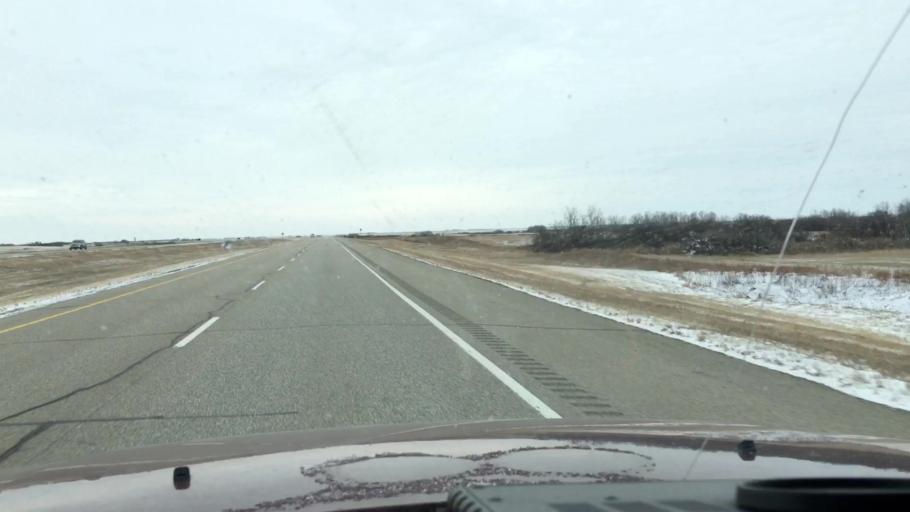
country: CA
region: Saskatchewan
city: Watrous
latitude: 51.3575
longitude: -106.1243
